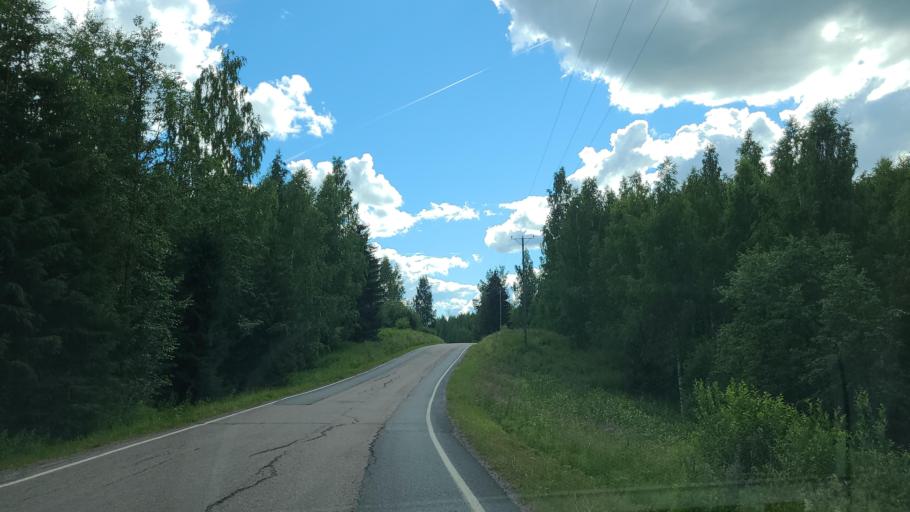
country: FI
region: Central Finland
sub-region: Jaemsae
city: Jaemsae
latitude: 61.8981
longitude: 25.2677
